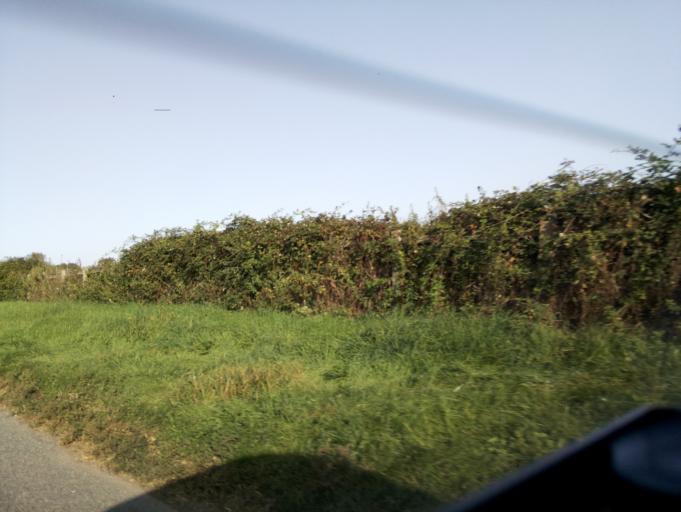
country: GB
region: England
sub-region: Gloucestershire
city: Tewkesbury
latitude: 51.9473
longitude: -2.1984
